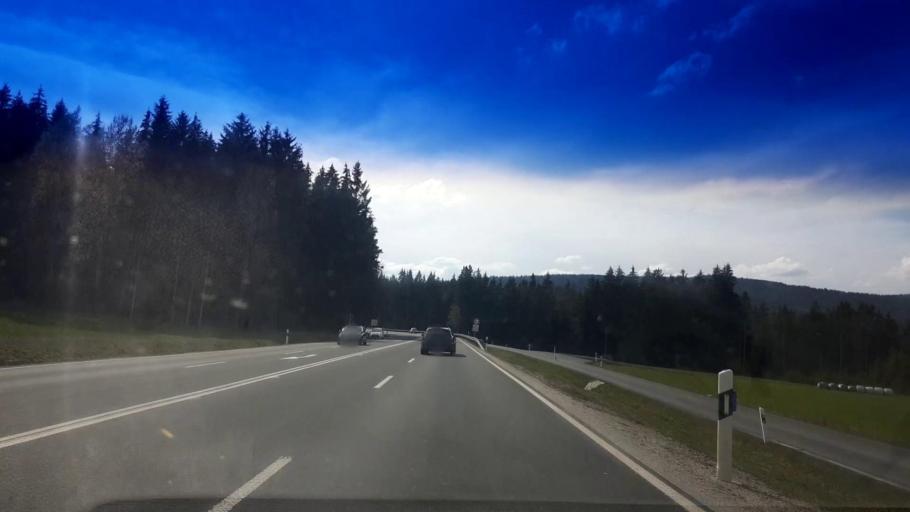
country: DE
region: Bavaria
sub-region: Upper Franconia
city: Trostau
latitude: 50.0177
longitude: 11.9320
